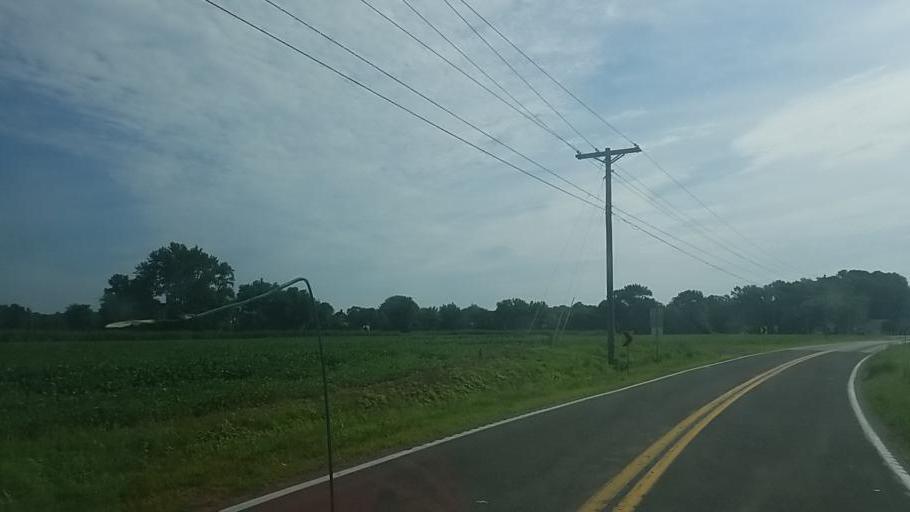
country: US
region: Delaware
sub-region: Sussex County
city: Ocean View
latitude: 38.5048
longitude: -75.1256
